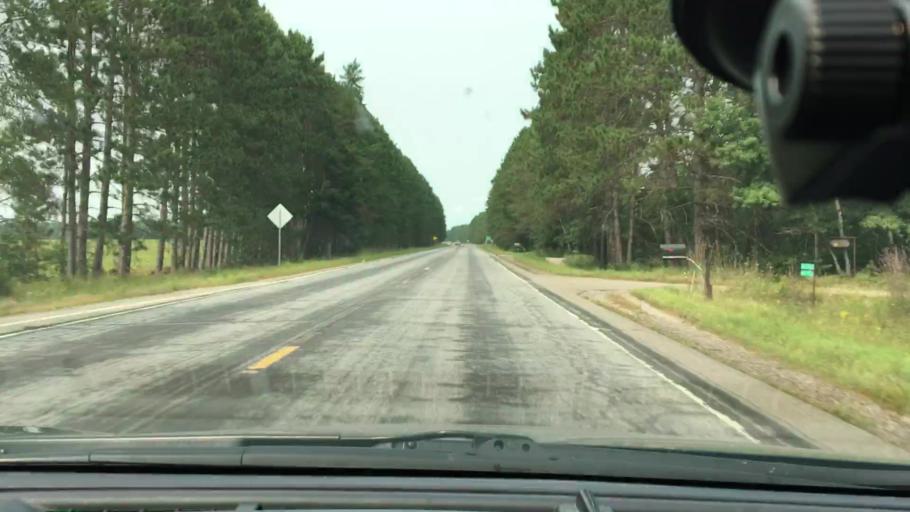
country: US
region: Minnesota
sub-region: Crow Wing County
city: Cross Lake
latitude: 46.7560
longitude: -93.9667
